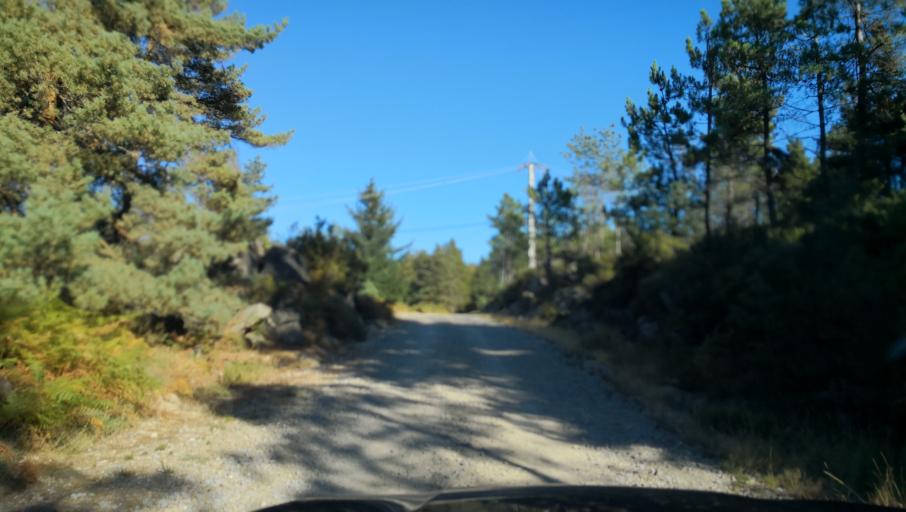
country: PT
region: Vila Real
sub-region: Vila Real
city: Vila Real
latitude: 41.3533
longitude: -7.7905
